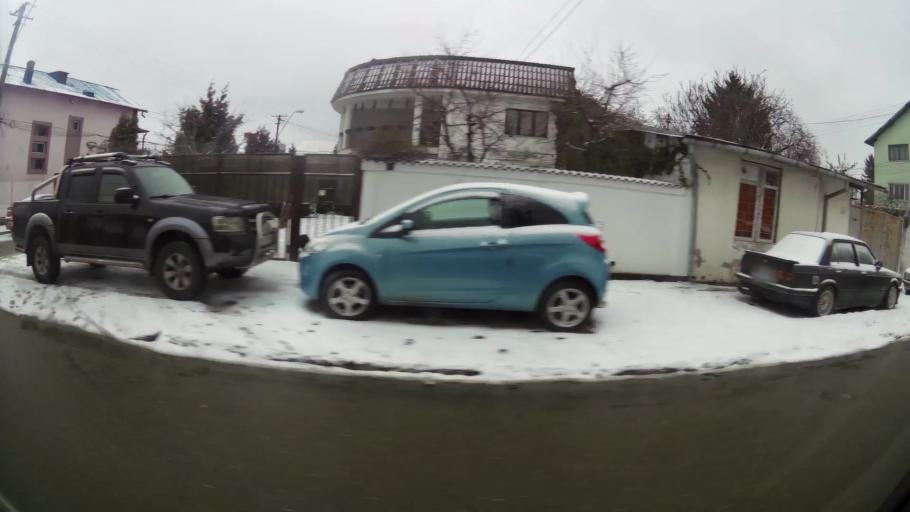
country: RO
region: Prahova
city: Ploiesti
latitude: 44.9315
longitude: 26.0381
